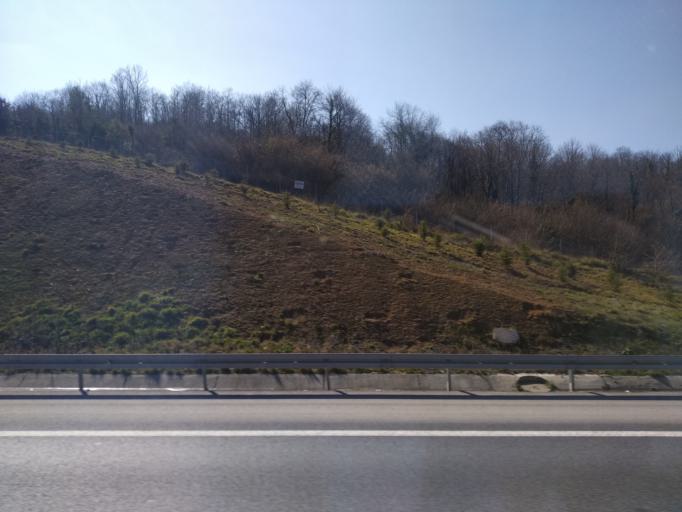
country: TR
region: Istanbul
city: Mahmut Sevket Pasa
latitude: 41.1673
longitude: 29.2530
